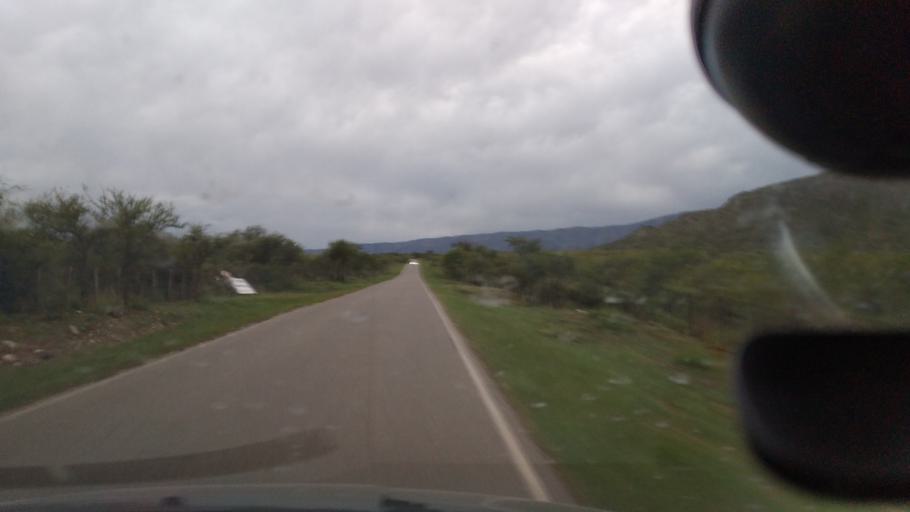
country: AR
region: Cordoba
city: Villa Las Rosas
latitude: -31.8878
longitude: -65.0292
